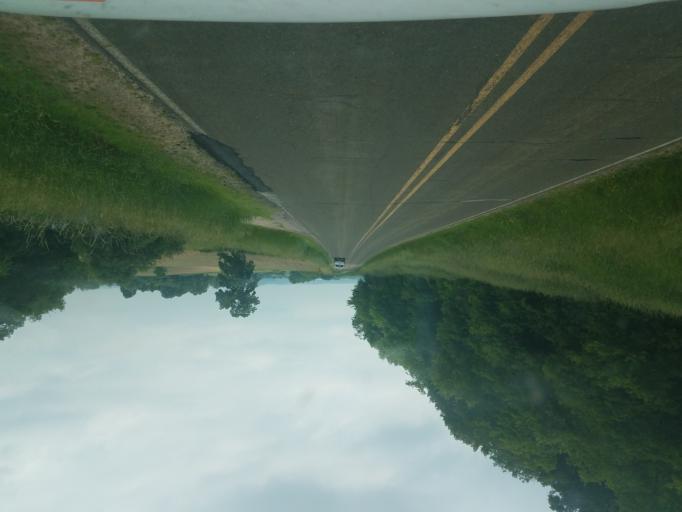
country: US
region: Wisconsin
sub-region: Vernon County
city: Hillsboro
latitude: 43.6461
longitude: -90.2897
